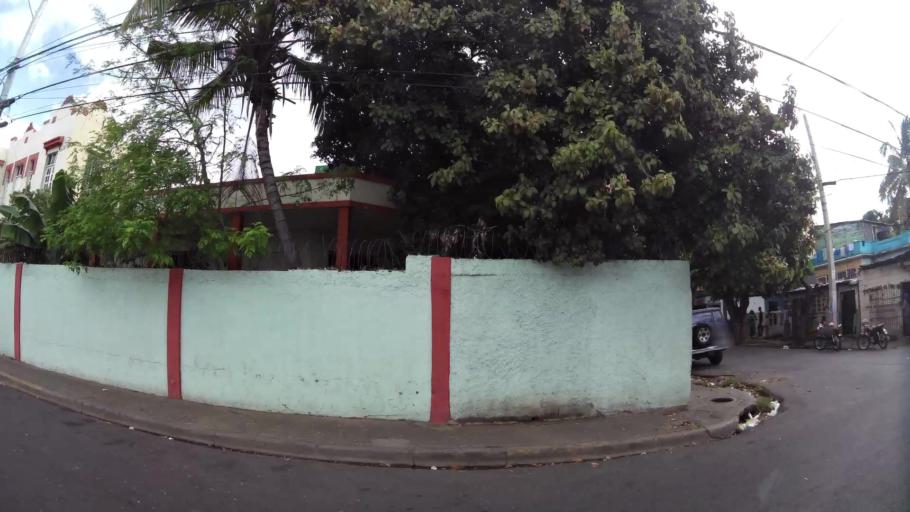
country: DO
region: Nacional
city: San Carlos
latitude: 18.4815
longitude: -69.8980
